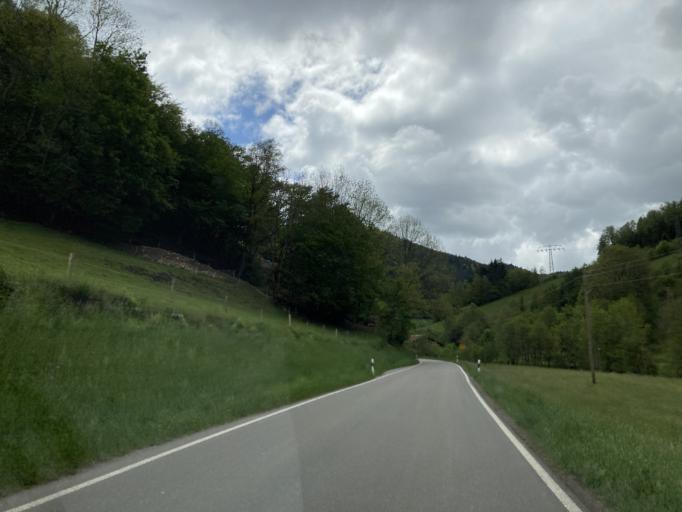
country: DE
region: Baden-Wuerttemberg
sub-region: Freiburg Region
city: Muhlenbach
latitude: 48.2070
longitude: 8.1562
